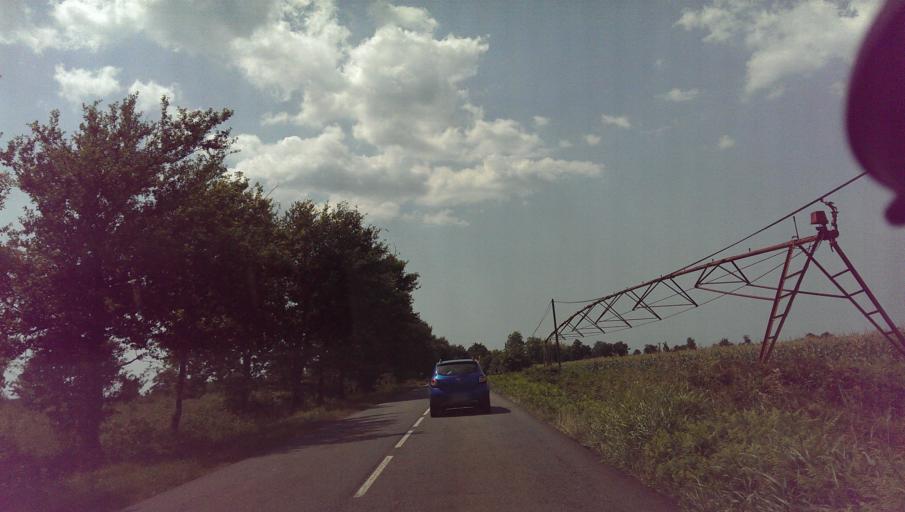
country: FR
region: Aquitaine
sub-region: Departement des Landes
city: Sabres
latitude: 44.1249
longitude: -0.6824
